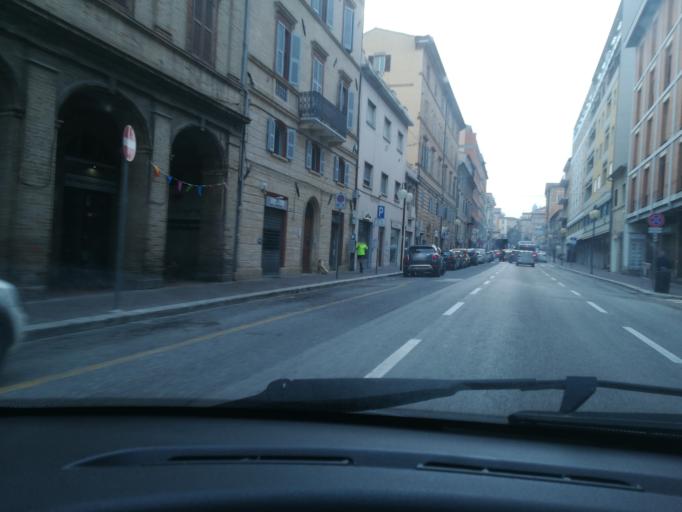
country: IT
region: The Marches
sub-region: Provincia di Macerata
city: Macerata
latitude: 43.3015
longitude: 13.4437
